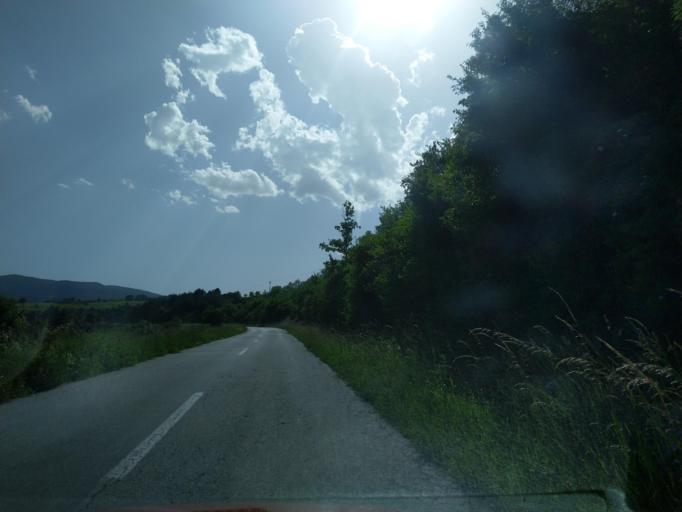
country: RS
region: Central Serbia
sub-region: Zlatiborski Okrug
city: Bajina Basta
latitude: 43.8452
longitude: 19.6092
